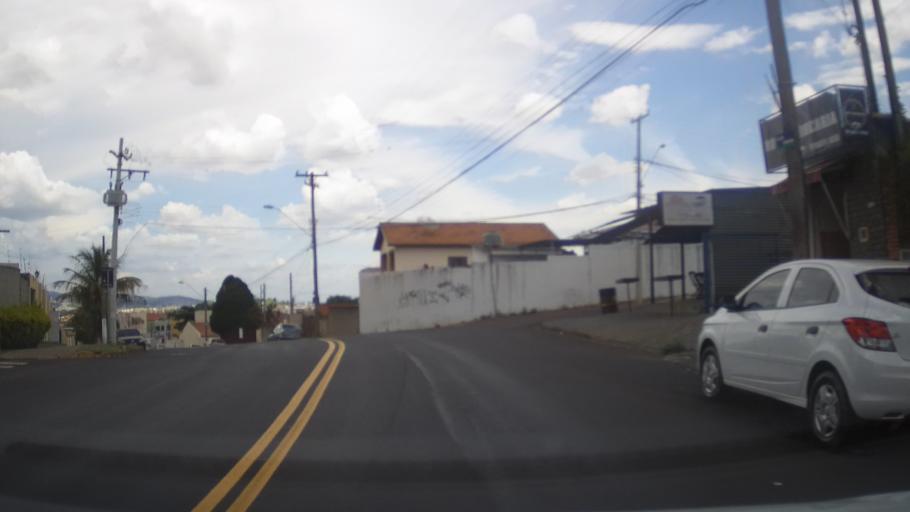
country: BR
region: Sao Paulo
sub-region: Campinas
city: Campinas
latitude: -22.9207
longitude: -47.0181
